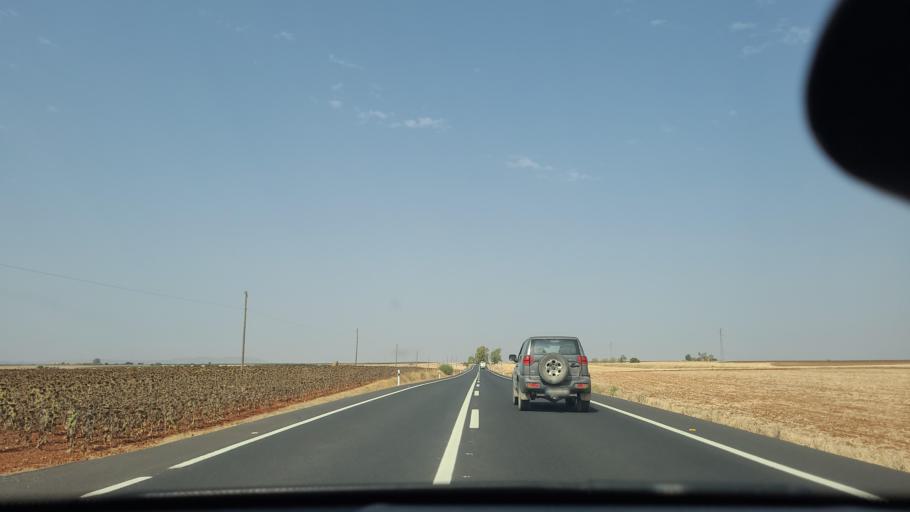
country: ES
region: Extremadura
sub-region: Provincia de Badajoz
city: Berlanga
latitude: 38.2652
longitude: -5.7546
